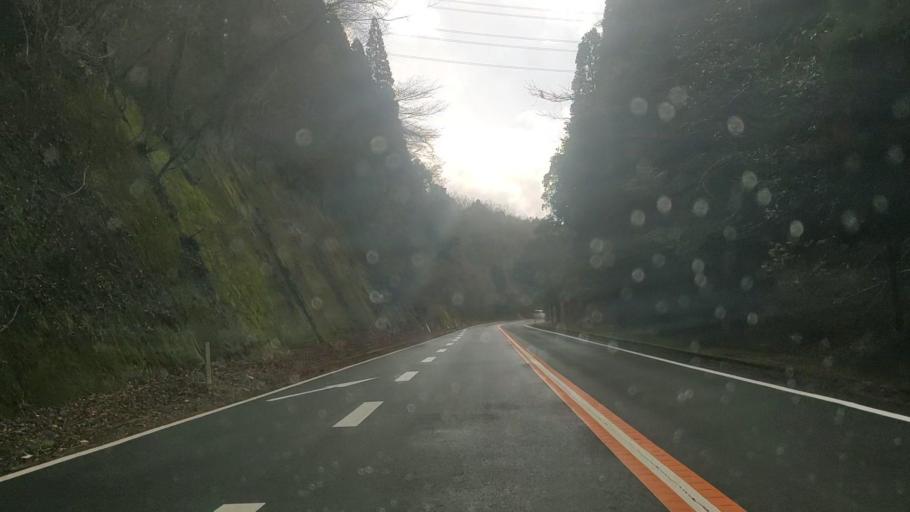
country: JP
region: Kumamoto
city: Hitoyoshi
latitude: 32.1103
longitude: 130.8055
